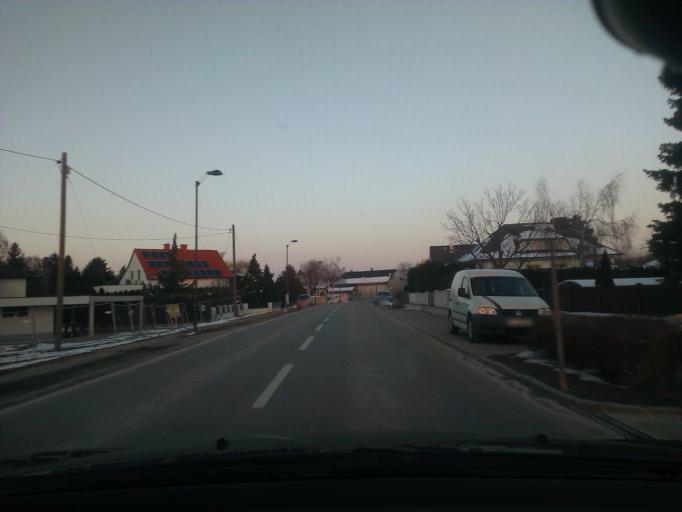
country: AT
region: Lower Austria
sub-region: Politischer Bezirk Bruck an der Leitha
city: Gotzendorf an der Leitha
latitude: 48.0108
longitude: 16.5725
